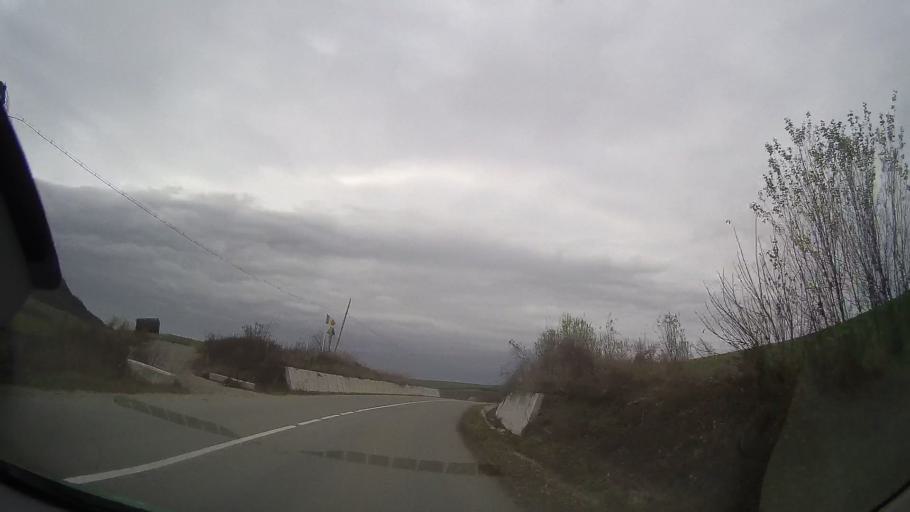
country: RO
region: Bistrita-Nasaud
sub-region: Comuna Milas
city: Milas
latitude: 46.7999
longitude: 24.4280
